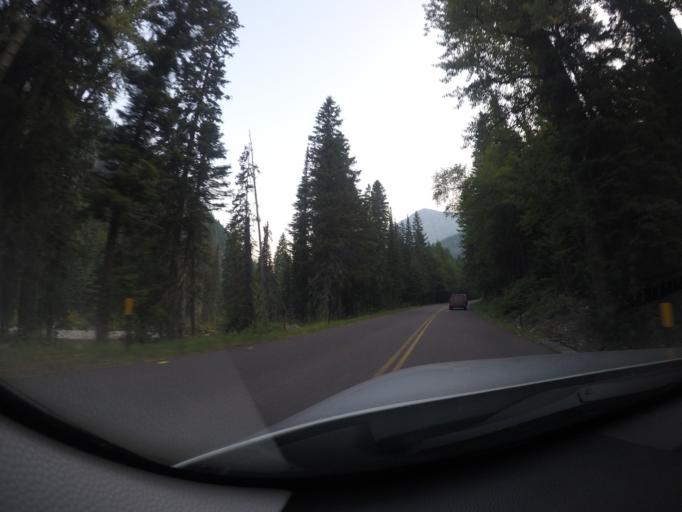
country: US
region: Montana
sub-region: Flathead County
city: Columbia Falls
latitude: 48.7306
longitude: -113.7622
